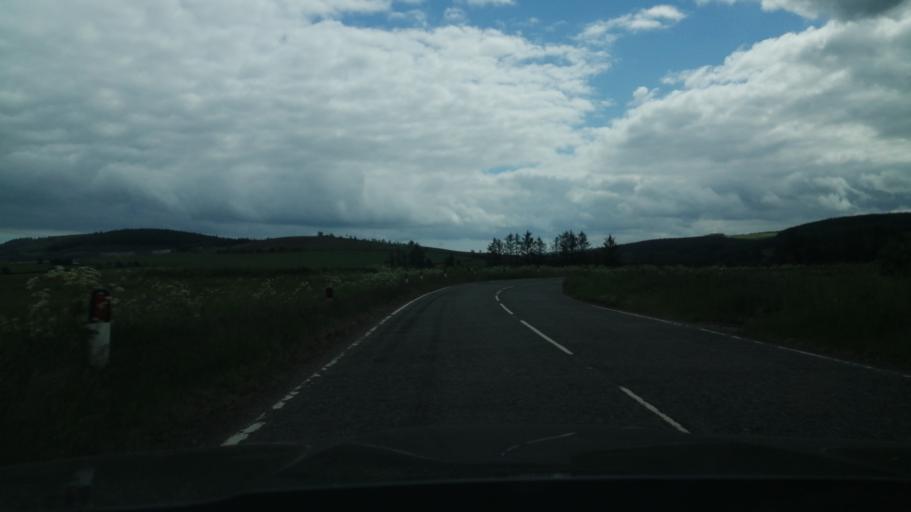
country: GB
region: Scotland
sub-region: Moray
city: Fochabers
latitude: 57.5451
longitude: -3.0883
